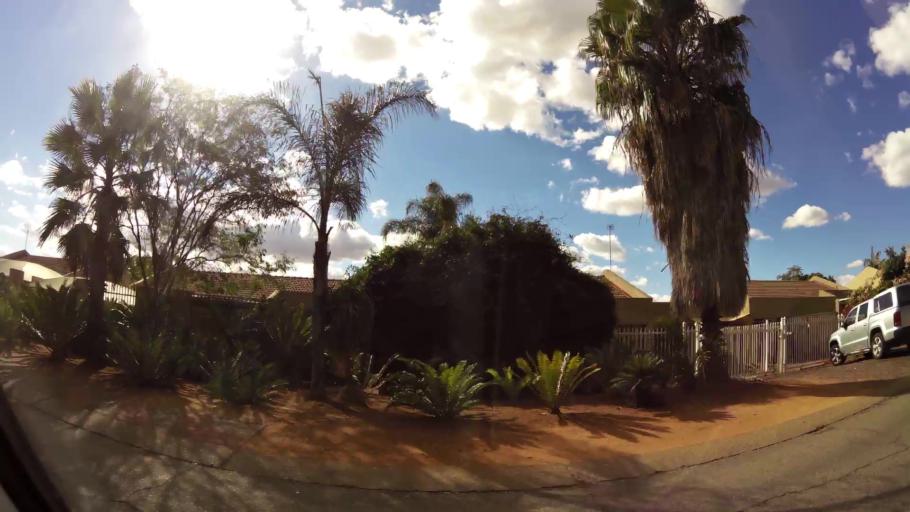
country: ZA
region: Limpopo
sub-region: Capricorn District Municipality
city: Polokwane
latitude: -23.8944
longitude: 29.4715
